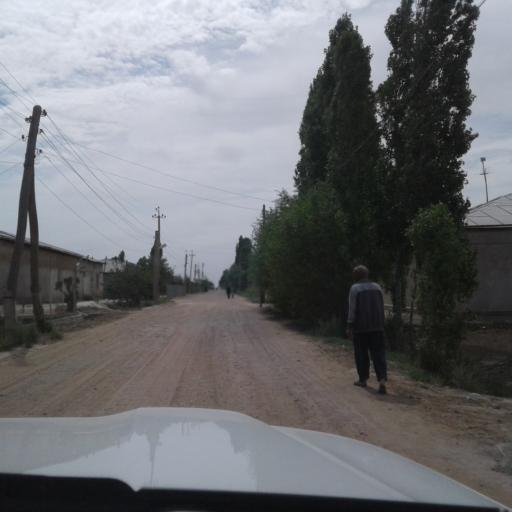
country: TM
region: Dasoguz
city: Tagta
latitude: 41.6010
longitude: 59.8487
